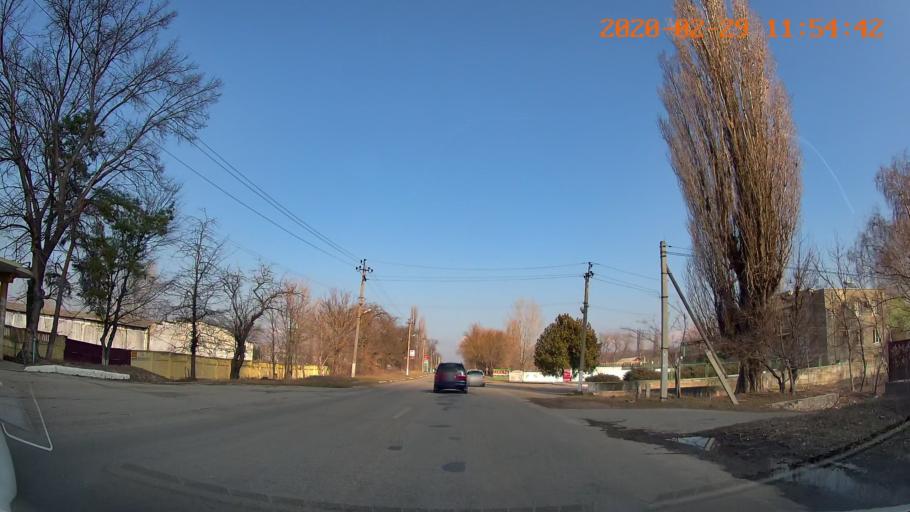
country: MD
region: Telenesti
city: Ribnita
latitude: 47.7858
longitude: 28.9959
